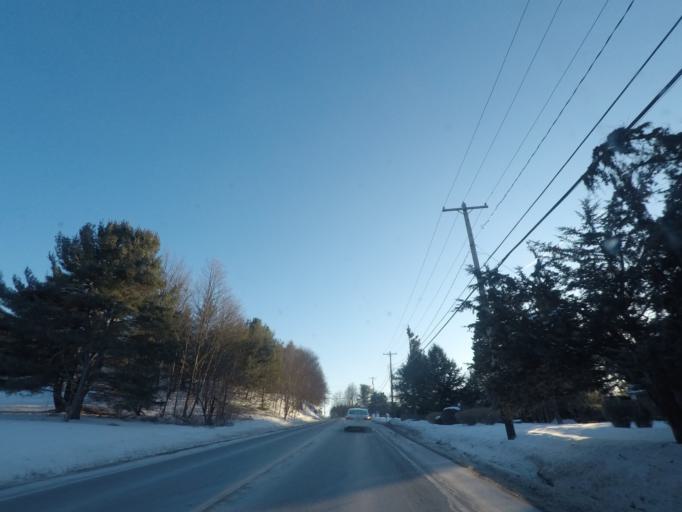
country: US
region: New York
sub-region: Saratoga County
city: Waterford
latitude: 42.8243
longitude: -73.6300
